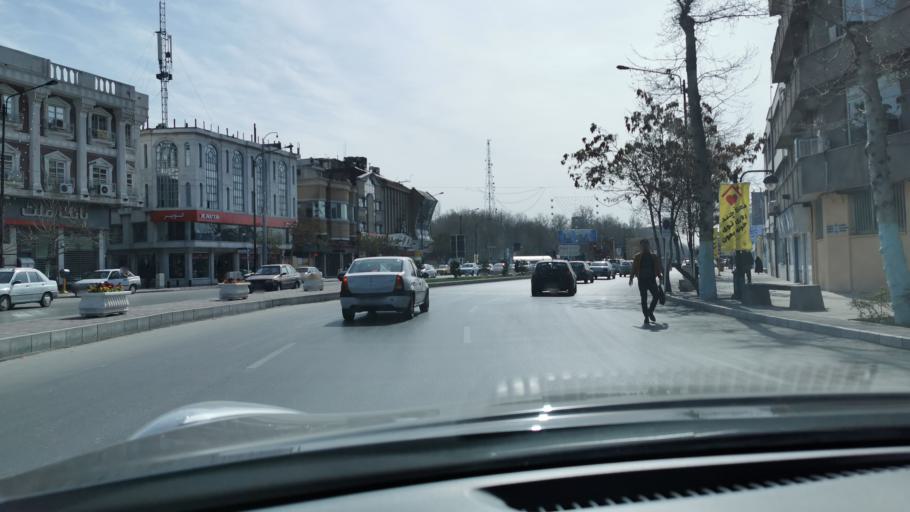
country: IR
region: Razavi Khorasan
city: Mashhad
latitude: 36.2922
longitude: 59.5847
